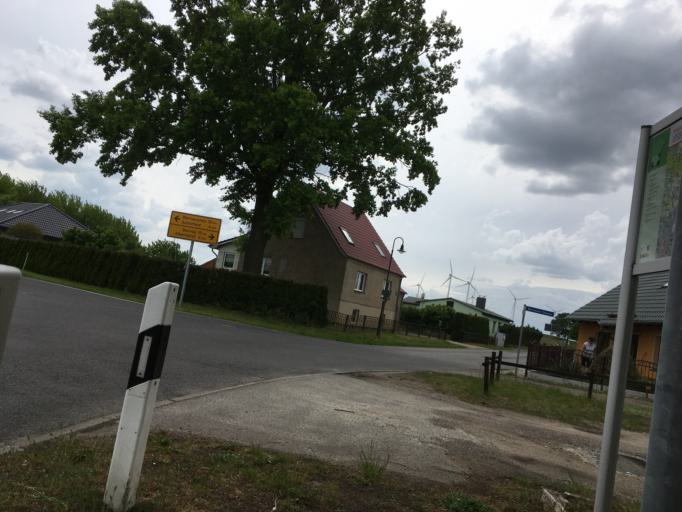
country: DE
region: Brandenburg
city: Melchow
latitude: 52.7082
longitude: 13.7182
